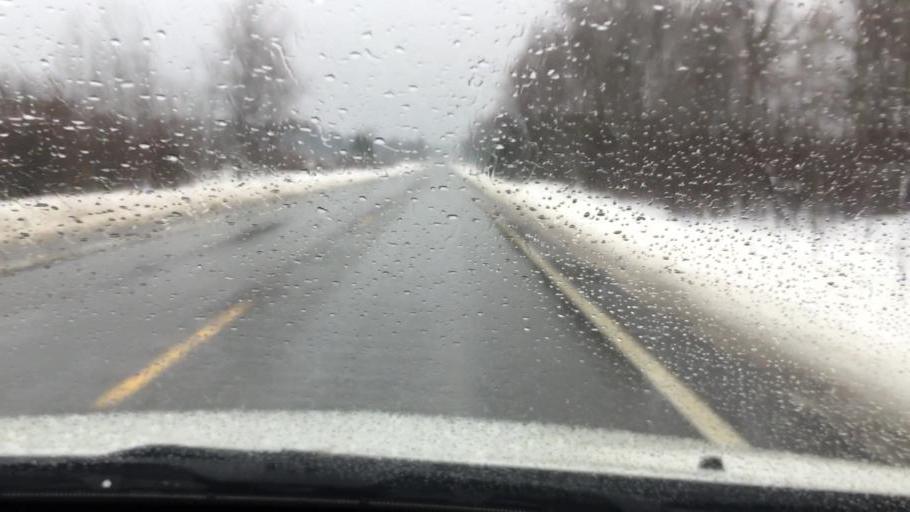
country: US
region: Michigan
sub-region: Charlevoix County
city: East Jordan
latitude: 45.0614
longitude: -85.0787
